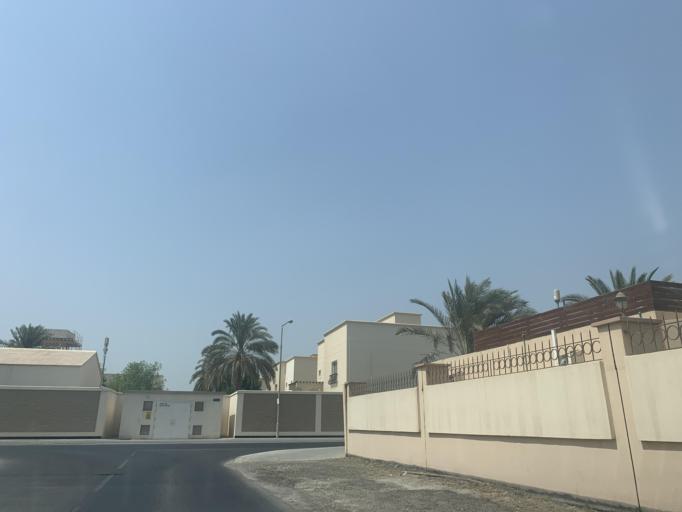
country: BH
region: Manama
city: Jidd Hafs
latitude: 26.2016
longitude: 50.4937
